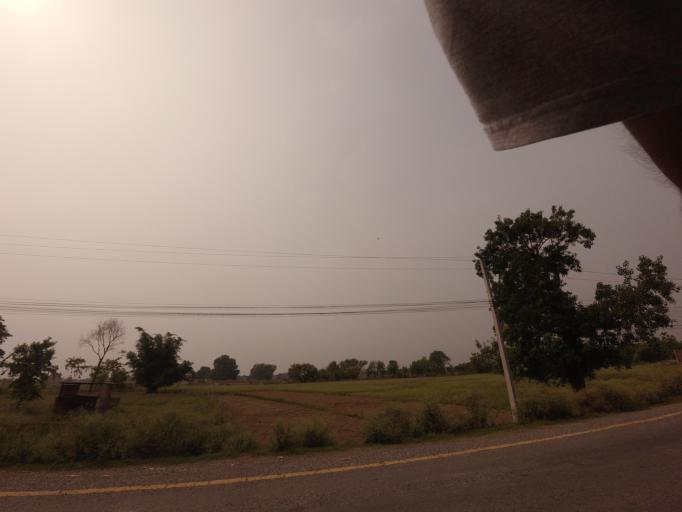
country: NP
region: Western Region
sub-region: Lumbini Zone
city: Bhairahawa
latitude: 27.5074
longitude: 83.3857
